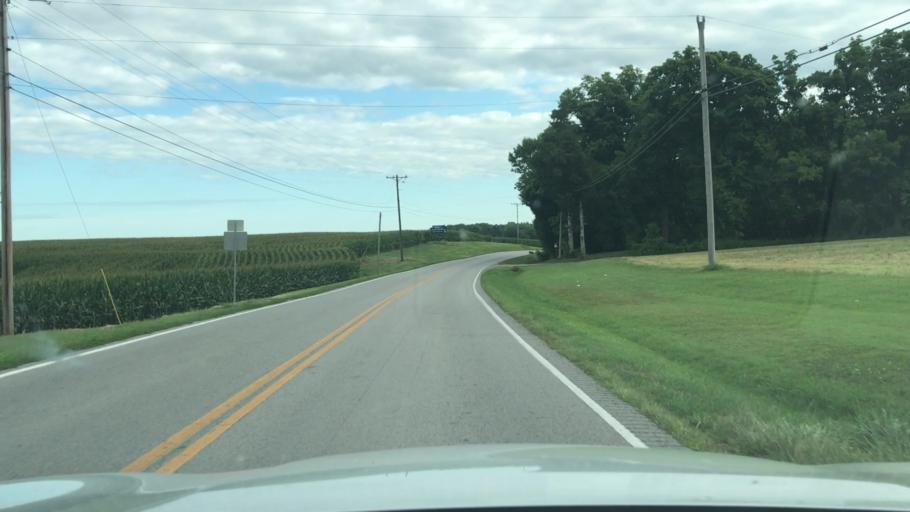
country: US
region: Kentucky
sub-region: Todd County
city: Elkton
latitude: 36.7891
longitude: -87.1642
